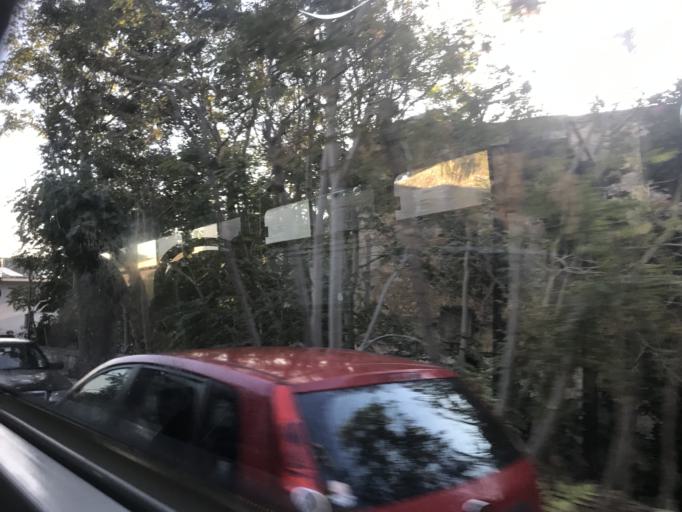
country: GR
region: Crete
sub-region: Nomos Irakleiou
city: Irakleion
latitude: 35.3377
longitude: 25.1375
